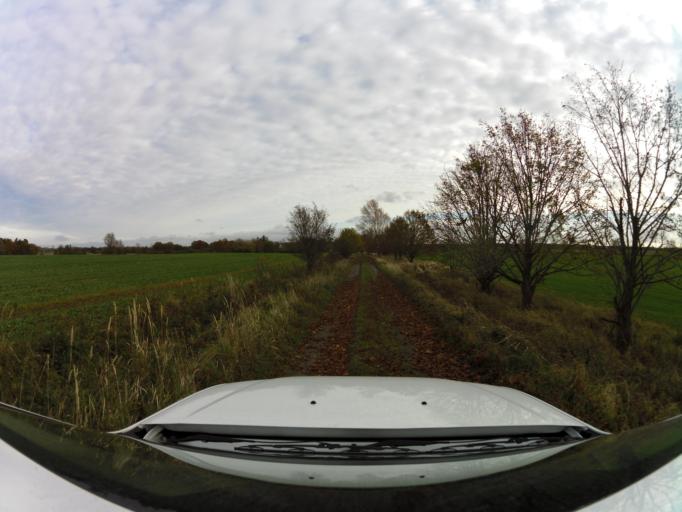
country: PL
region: West Pomeranian Voivodeship
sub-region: Powiat gryficki
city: Karnice
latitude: 54.0515
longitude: 15.0949
